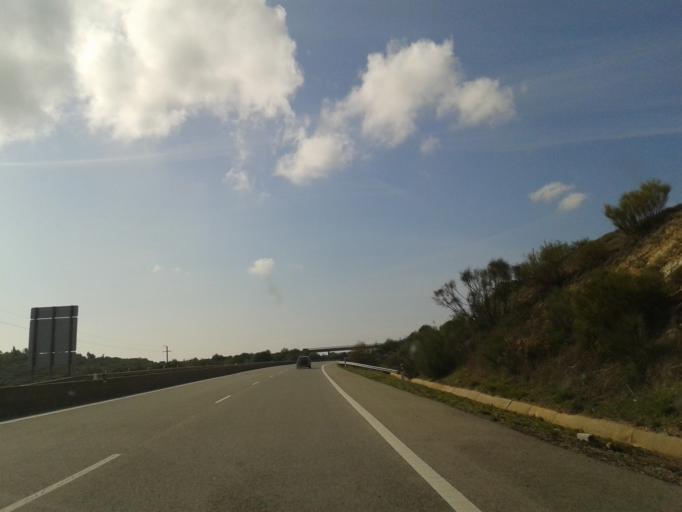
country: PT
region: Faro
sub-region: Olhao
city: Moncarapacho
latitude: 37.0935
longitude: -7.8139
